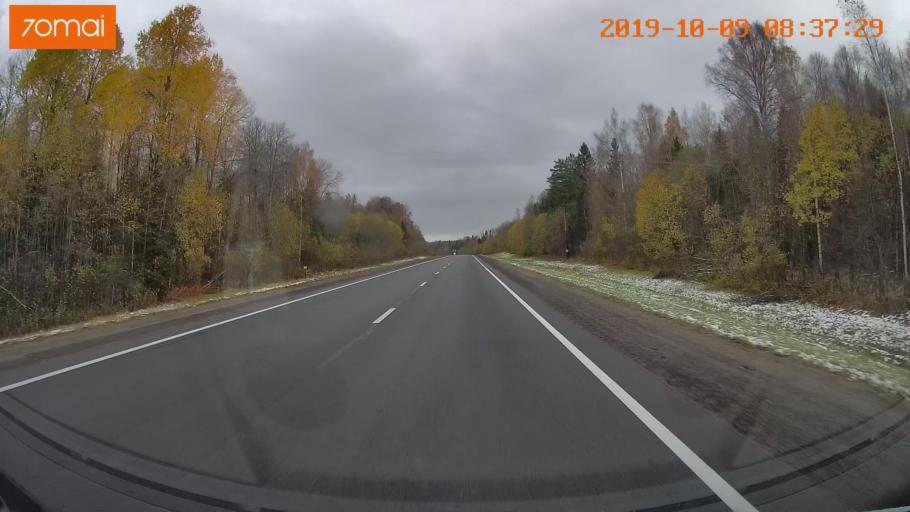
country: RU
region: Vologda
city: Gryazovets
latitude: 58.9421
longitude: 40.1743
